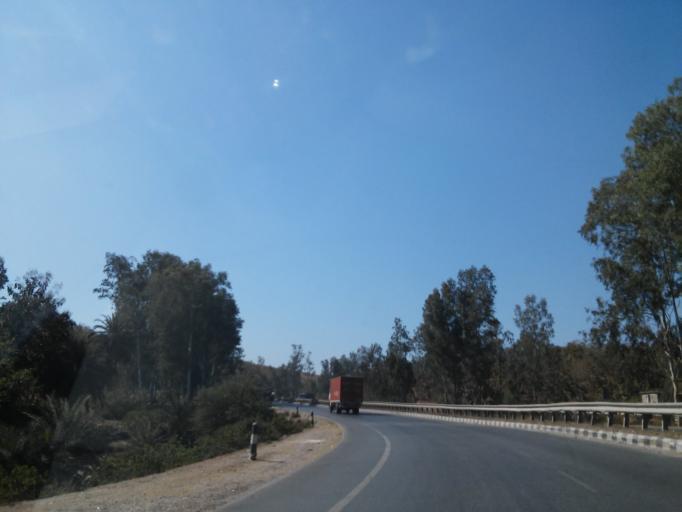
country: IN
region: Rajasthan
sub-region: Dungarpur
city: Dungarpur
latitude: 23.7743
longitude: 73.5062
